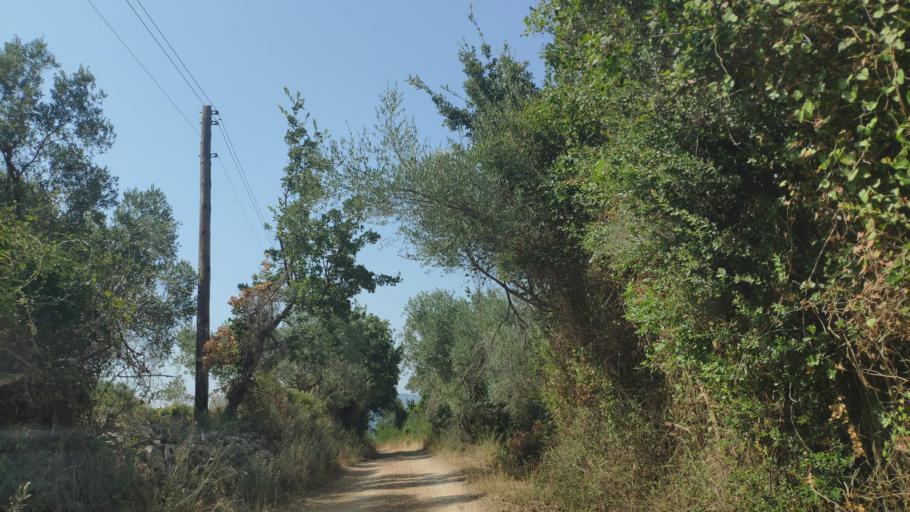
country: GR
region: West Greece
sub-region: Nomos Aitolias kai Akarnanias
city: Fitiai
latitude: 38.7184
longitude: 21.1955
